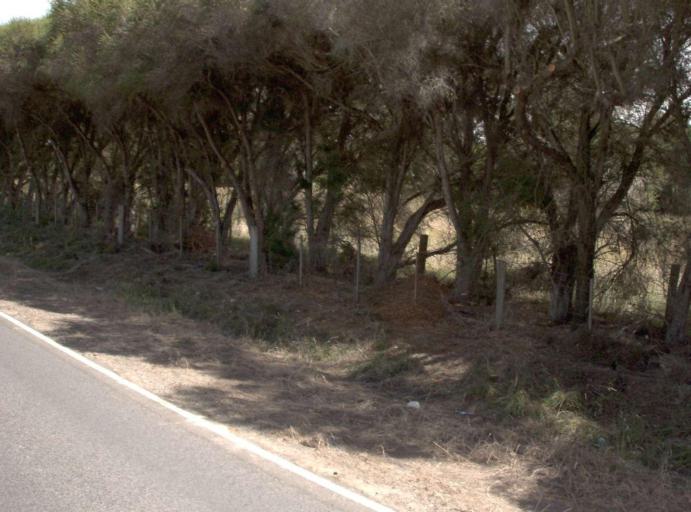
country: AU
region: Victoria
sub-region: Wellington
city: Heyfield
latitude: -38.0723
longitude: 146.8704
